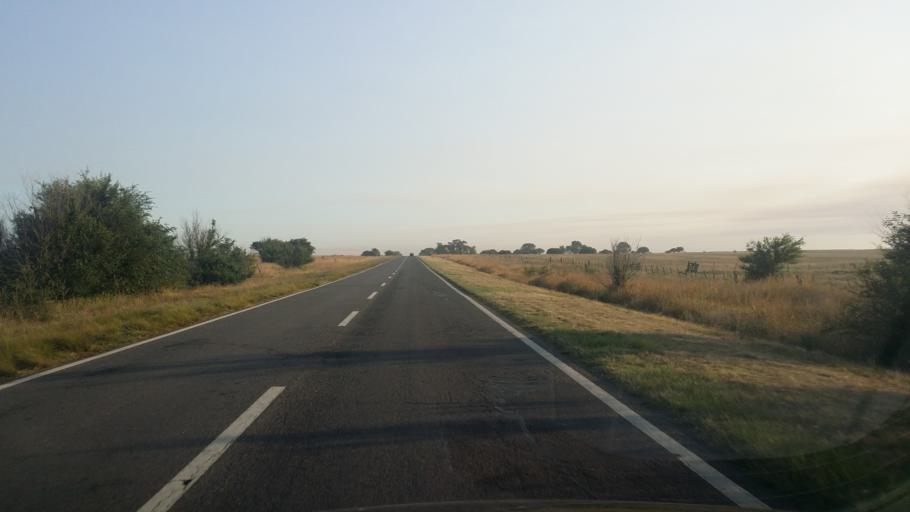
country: AR
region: La Pampa
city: Santa Rosa
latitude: -36.4535
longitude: -64.2800
